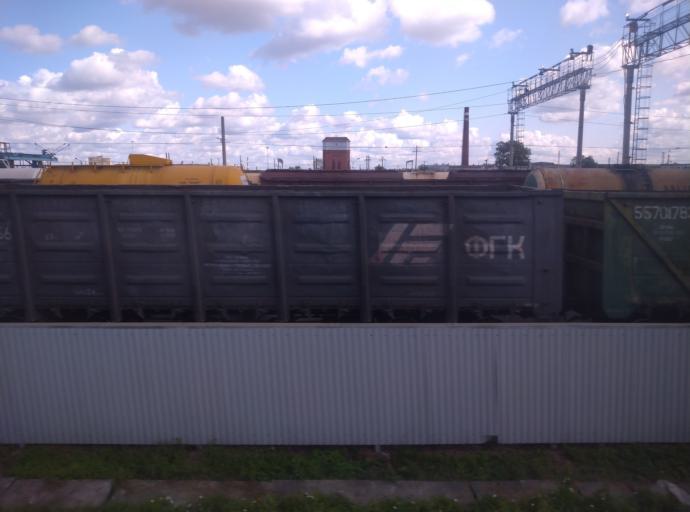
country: RU
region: St.-Petersburg
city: Obukhovo
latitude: 59.8715
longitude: 30.4178
